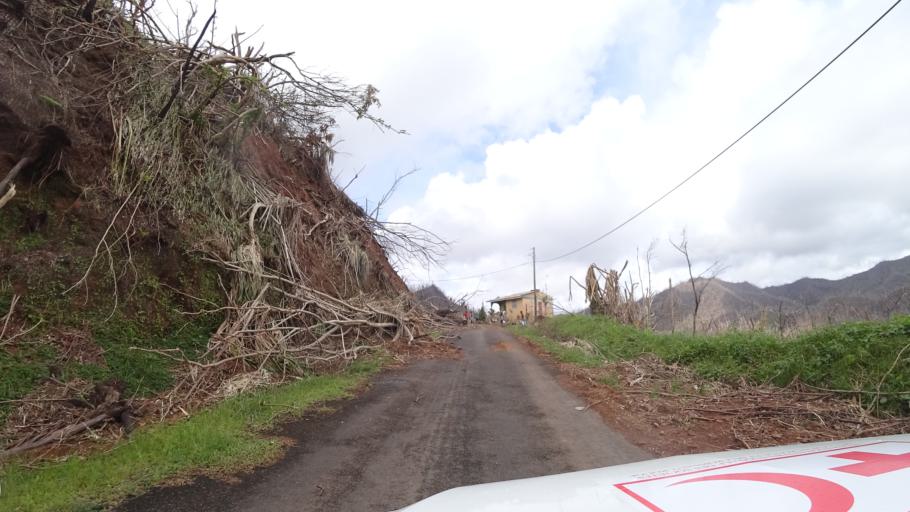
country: DM
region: Saint David
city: Rosalie
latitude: 15.3946
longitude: -61.2607
